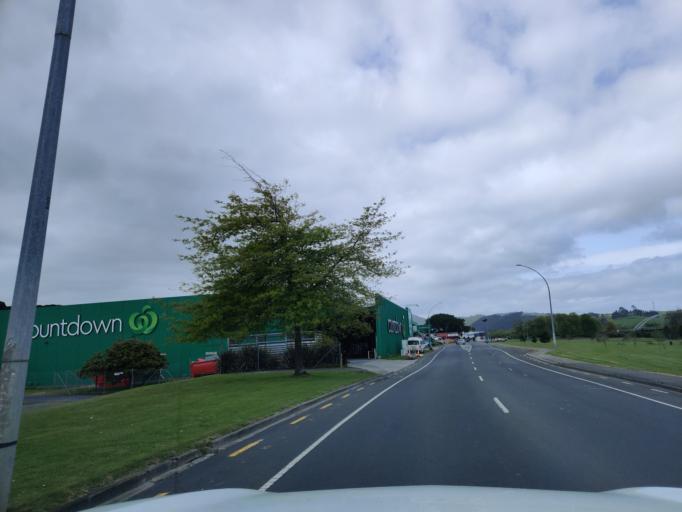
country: NZ
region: Waikato
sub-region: Waikato District
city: Ngaruawahia
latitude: -37.5632
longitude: 175.1585
